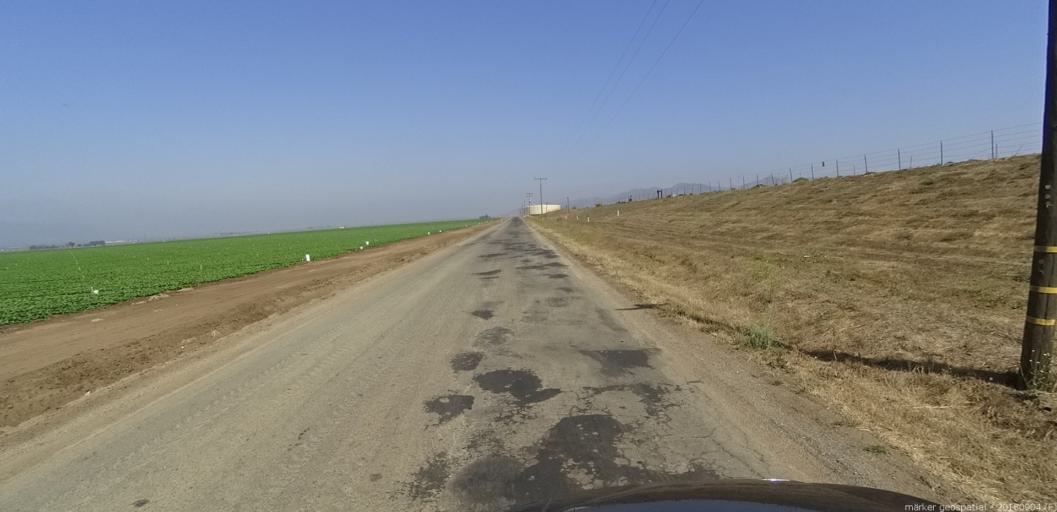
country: US
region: California
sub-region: Monterey County
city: Gonzales
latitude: 36.5212
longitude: -121.4141
